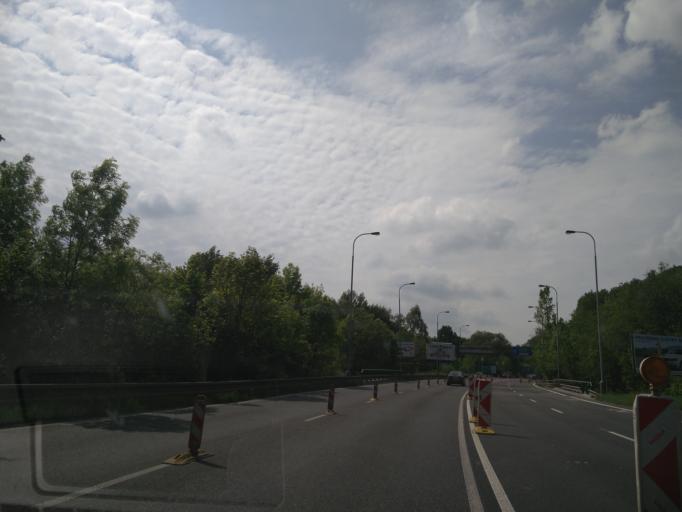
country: CZ
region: Central Bohemia
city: Horomerice
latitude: 50.0652
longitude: 14.3351
